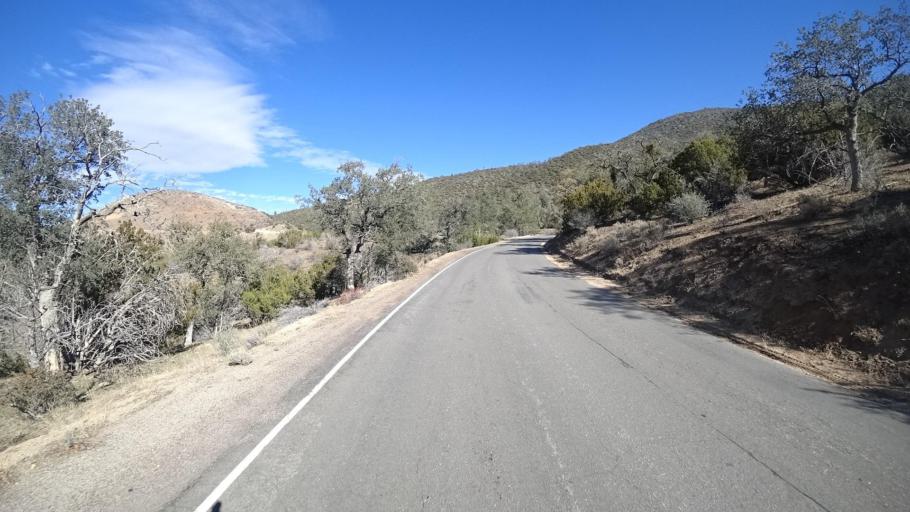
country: US
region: California
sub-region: Kern County
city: Bodfish
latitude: 35.5608
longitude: -118.5069
